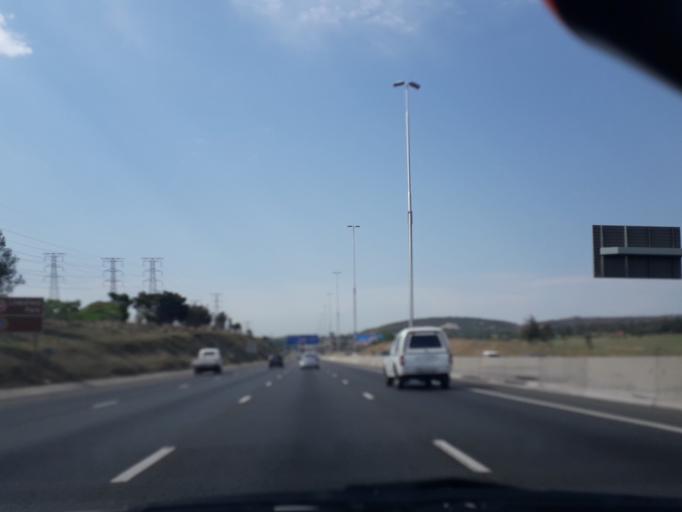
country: ZA
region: Gauteng
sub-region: City of Johannesburg Metropolitan Municipality
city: Modderfontein
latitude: -26.1378
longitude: 28.1330
